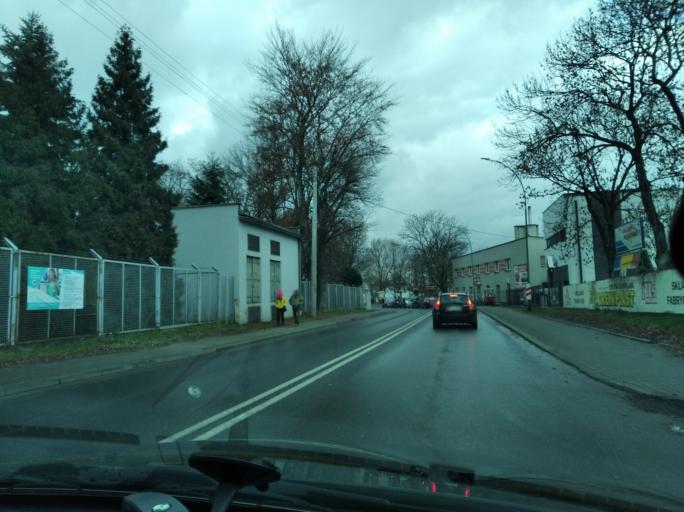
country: PL
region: Subcarpathian Voivodeship
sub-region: Powiat lancucki
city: Lancut
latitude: 50.0796
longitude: 22.2329
